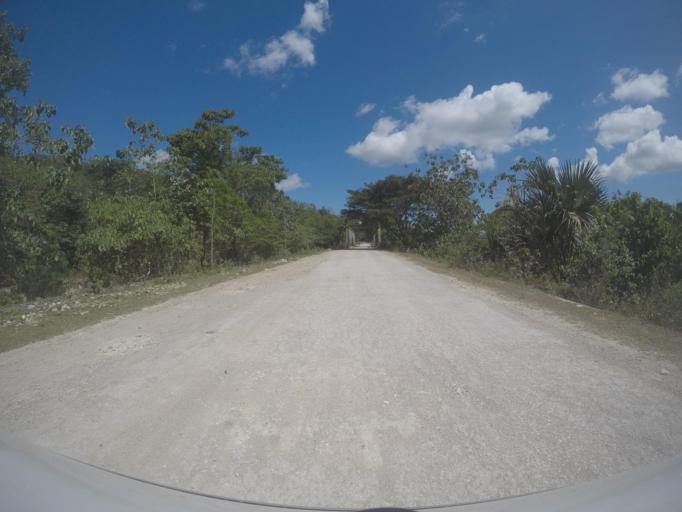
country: TL
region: Viqueque
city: Viqueque
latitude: -8.9011
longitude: 126.3929
